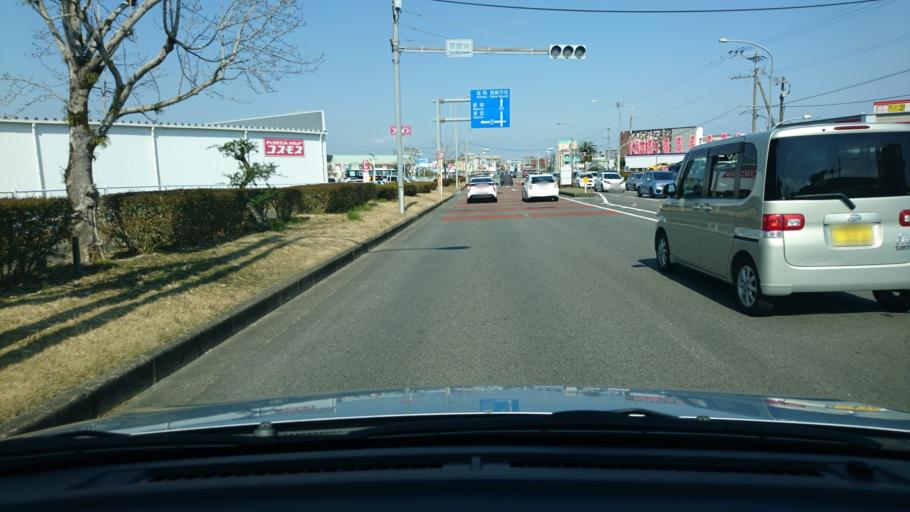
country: JP
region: Miyazaki
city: Miyazaki-shi
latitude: 31.8863
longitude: 131.4117
